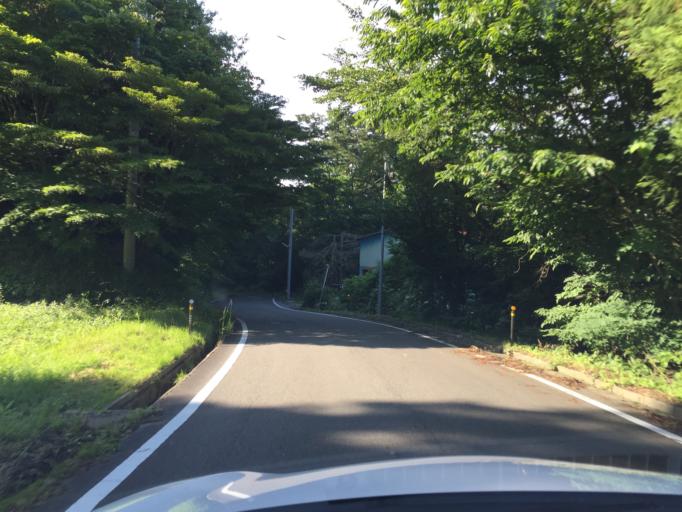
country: JP
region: Fukushima
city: Sukagawa
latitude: 37.2658
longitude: 140.5006
